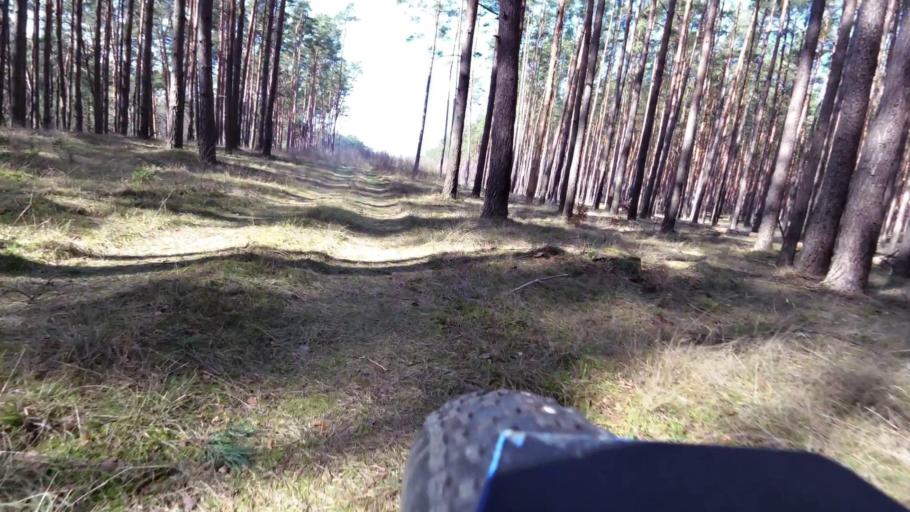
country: PL
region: Lubusz
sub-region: Powiat slubicki
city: Cybinka
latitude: 52.2098
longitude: 14.9203
